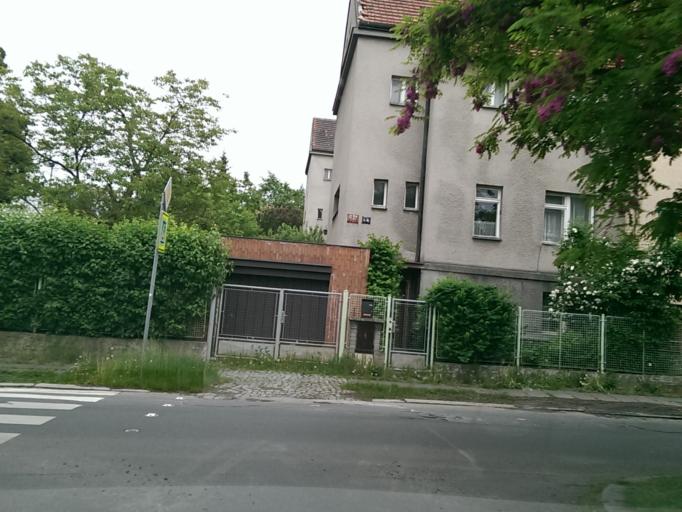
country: CZ
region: Praha
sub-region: Praha 8
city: Karlin
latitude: 50.0443
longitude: 14.4781
